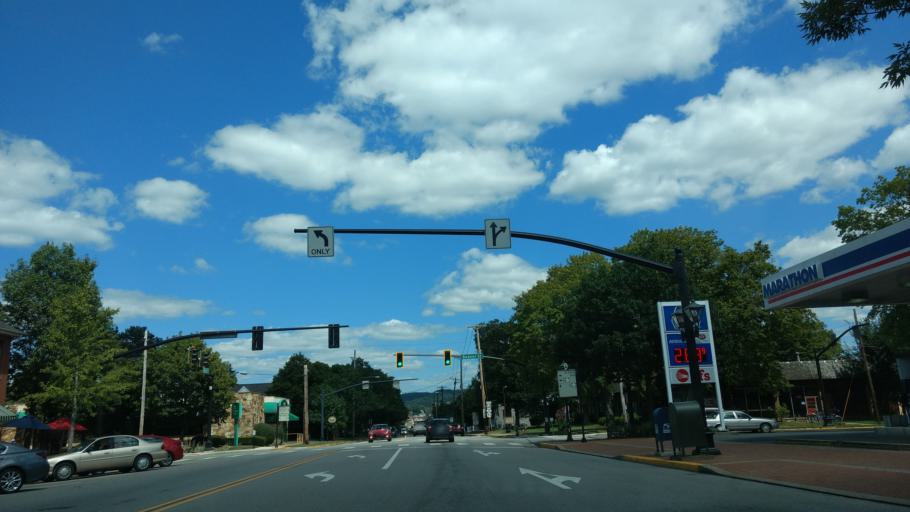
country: US
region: Pennsylvania
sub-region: Beaver County
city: Beaver
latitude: 40.6963
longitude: -80.3022
